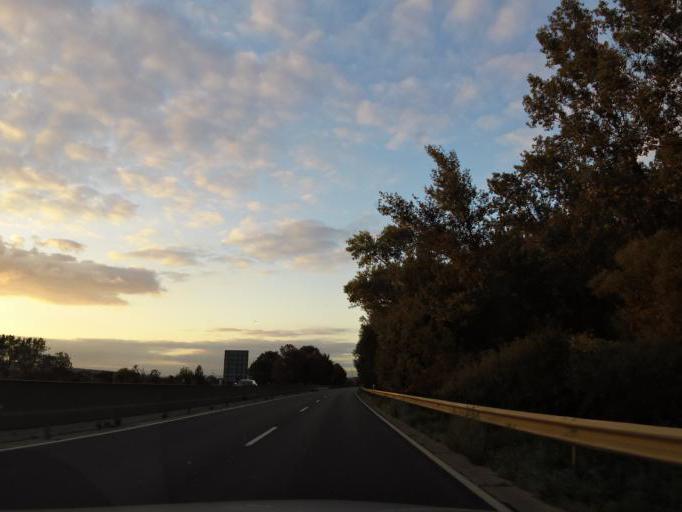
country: DE
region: Rheinland-Pfalz
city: Bodenheim
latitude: 49.9376
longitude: 8.3401
